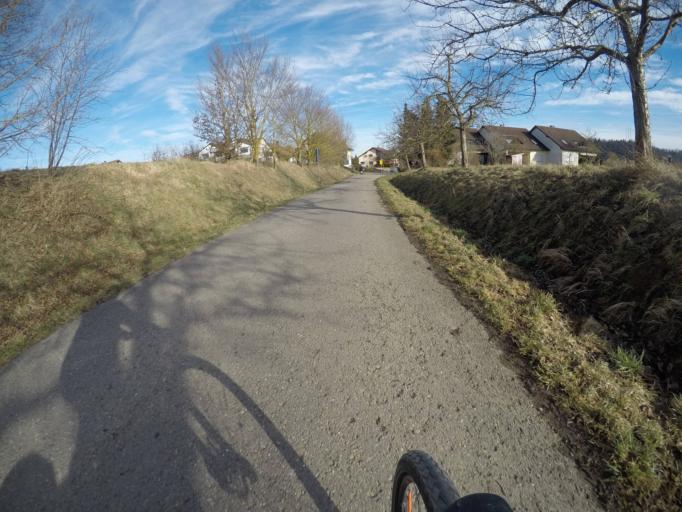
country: DE
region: Baden-Wuerttemberg
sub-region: Regierungsbezirk Stuttgart
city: Nufringen
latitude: 48.6224
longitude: 8.8791
